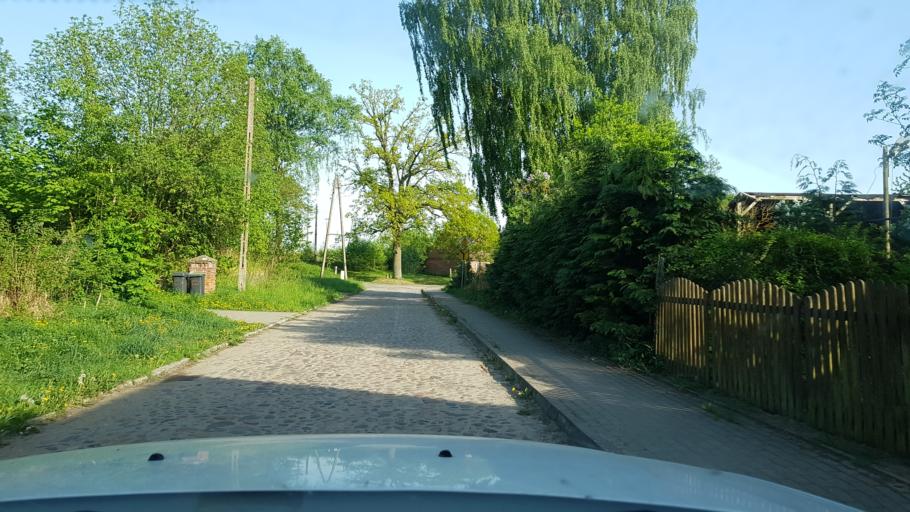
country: PL
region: West Pomeranian Voivodeship
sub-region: Powiat lobeski
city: Resko
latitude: 53.7062
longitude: 15.3357
